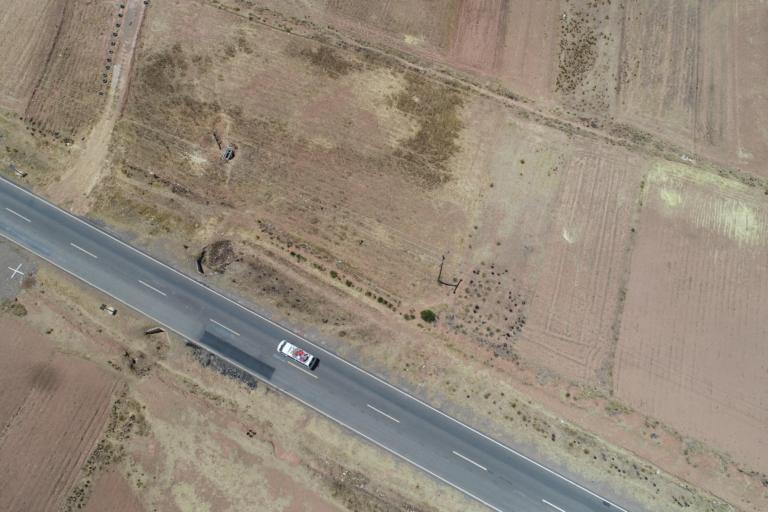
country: BO
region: La Paz
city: Achacachi
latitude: -15.9105
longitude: -68.8875
